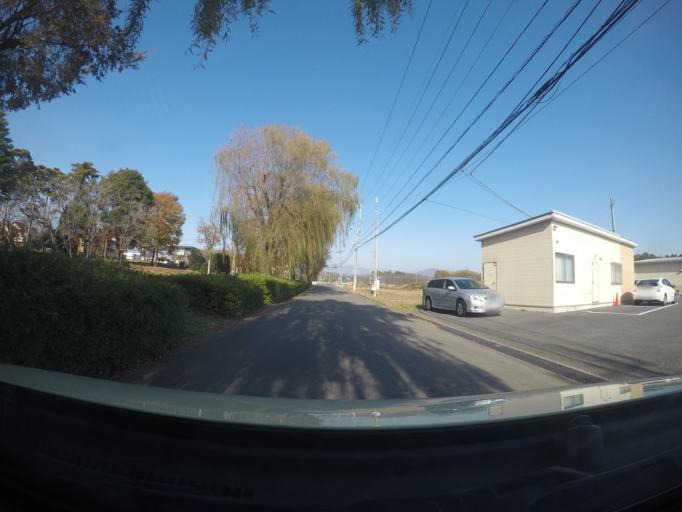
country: JP
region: Ibaraki
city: Naka
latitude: 36.1054
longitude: 140.1119
